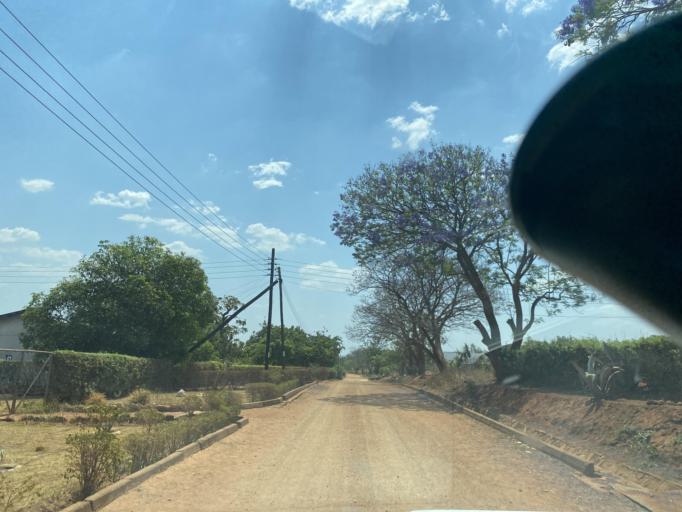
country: ZM
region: Lusaka
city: Kafue
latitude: -15.5061
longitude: 27.9361
